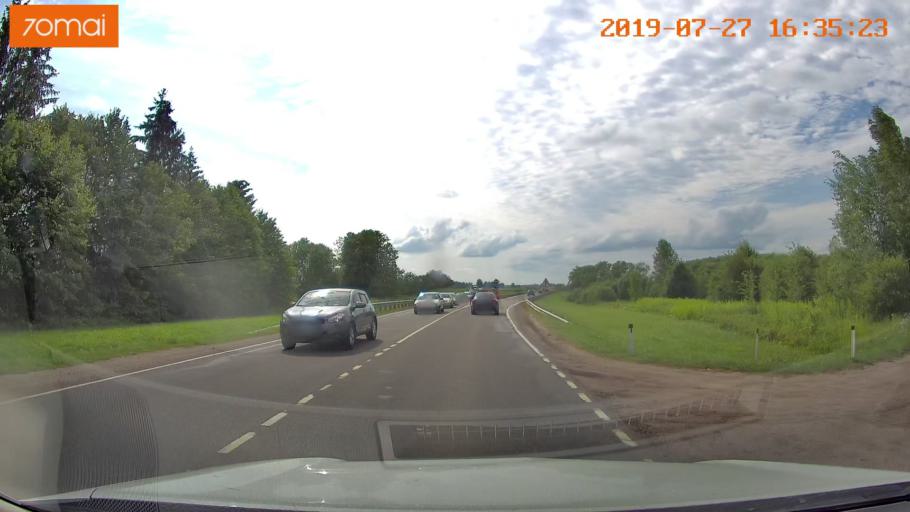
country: RU
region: Kaliningrad
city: Gvardeysk
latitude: 54.6493
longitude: 21.3095
